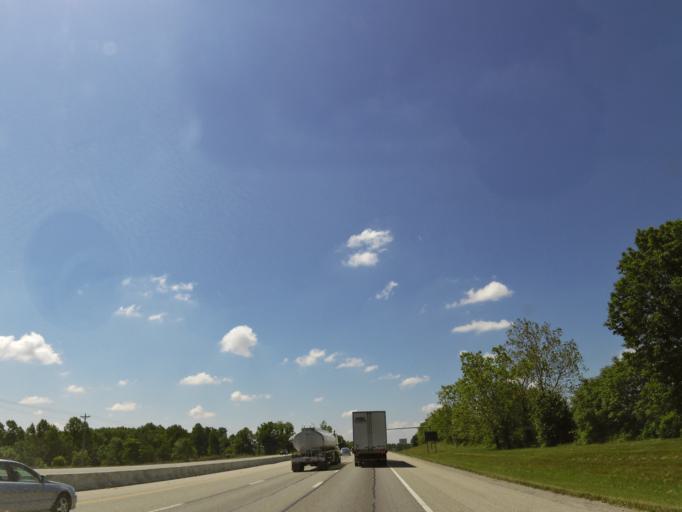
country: US
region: Kentucky
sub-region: Laurel County
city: London
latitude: 37.0637
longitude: -84.0984
